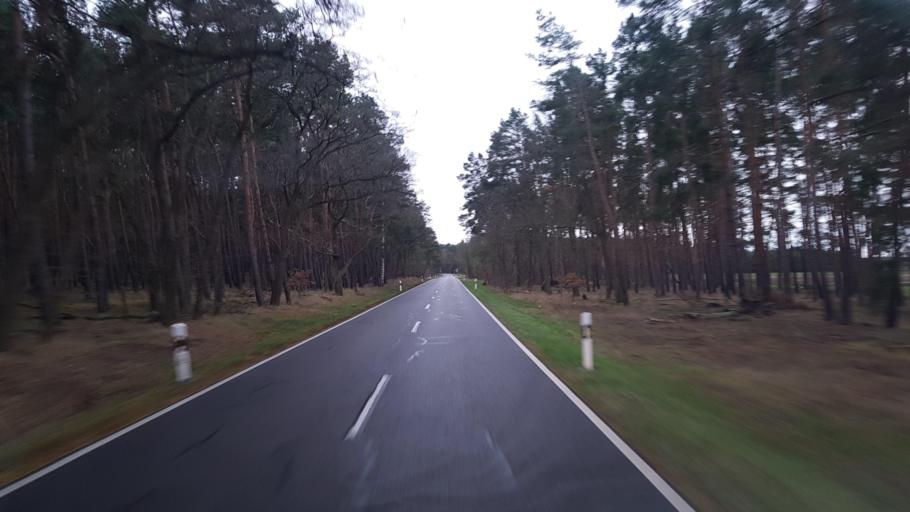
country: DE
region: Brandenburg
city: Schlepzig
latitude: 52.0096
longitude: 13.9753
